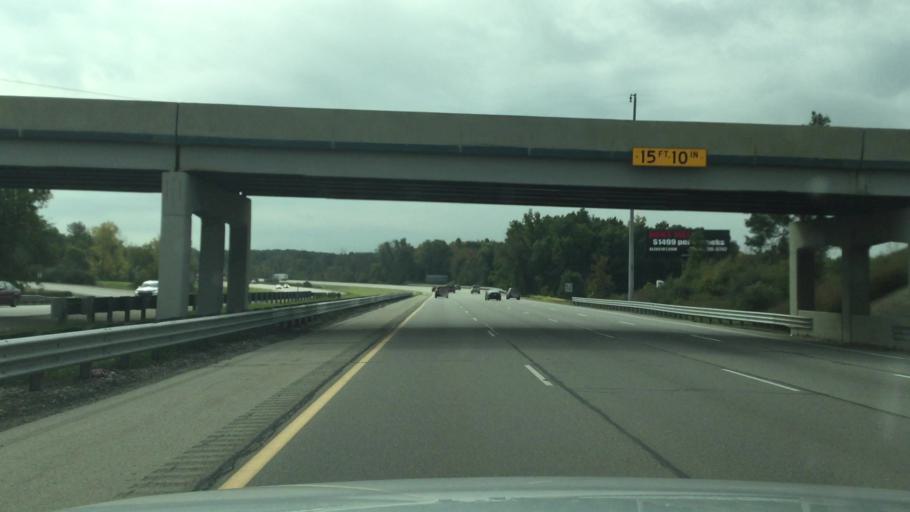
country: US
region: Michigan
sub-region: Oakland County
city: Holly
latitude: 42.8158
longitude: -83.5699
